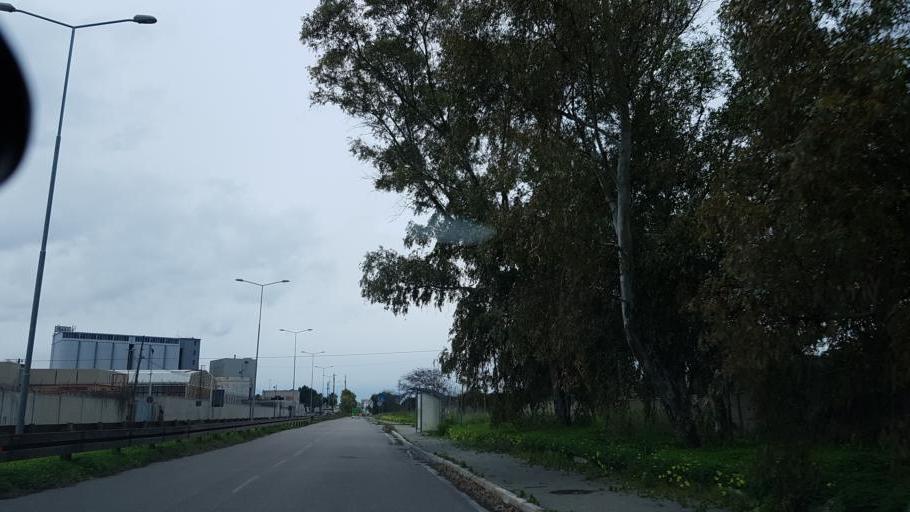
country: IT
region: Apulia
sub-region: Provincia di Brindisi
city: Materdomini
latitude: 40.6386
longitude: 17.9586
